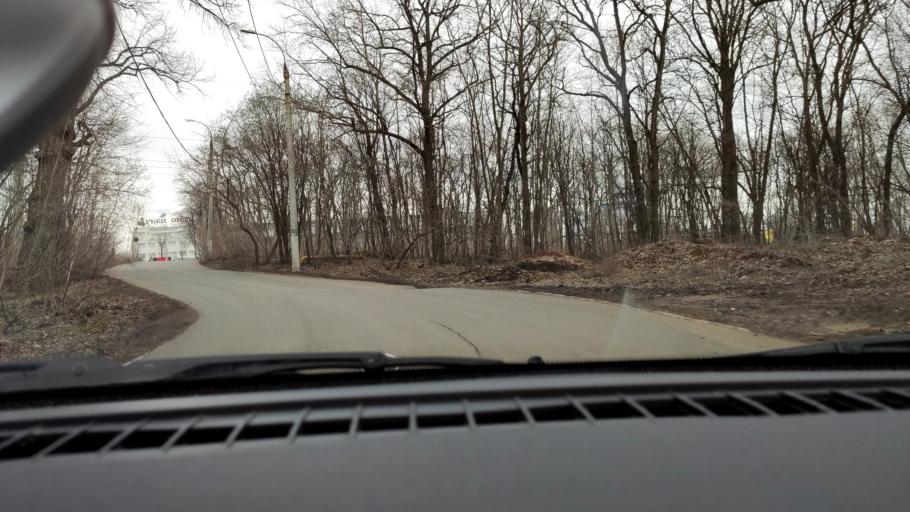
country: RU
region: Samara
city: Samara
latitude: 53.2742
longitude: 50.2231
